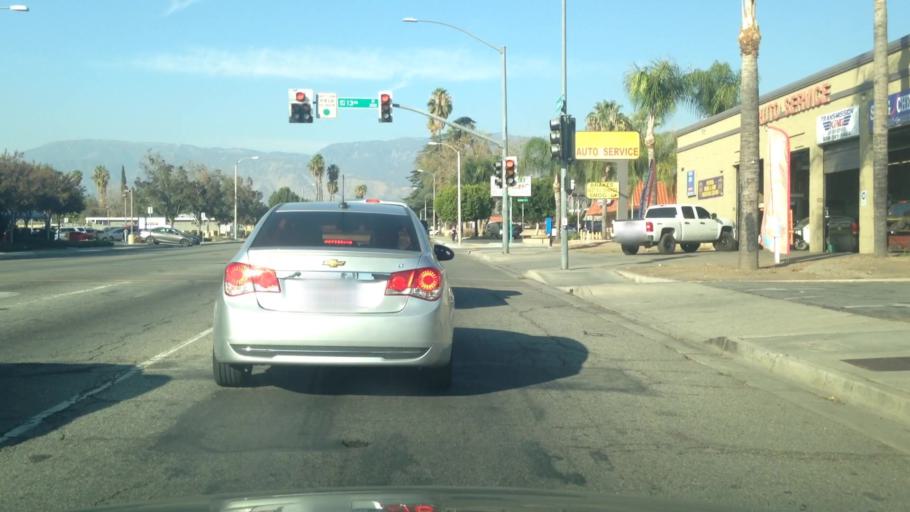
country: US
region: California
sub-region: San Bernardino County
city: San Bernardino
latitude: 34.1231
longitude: -117.2787
